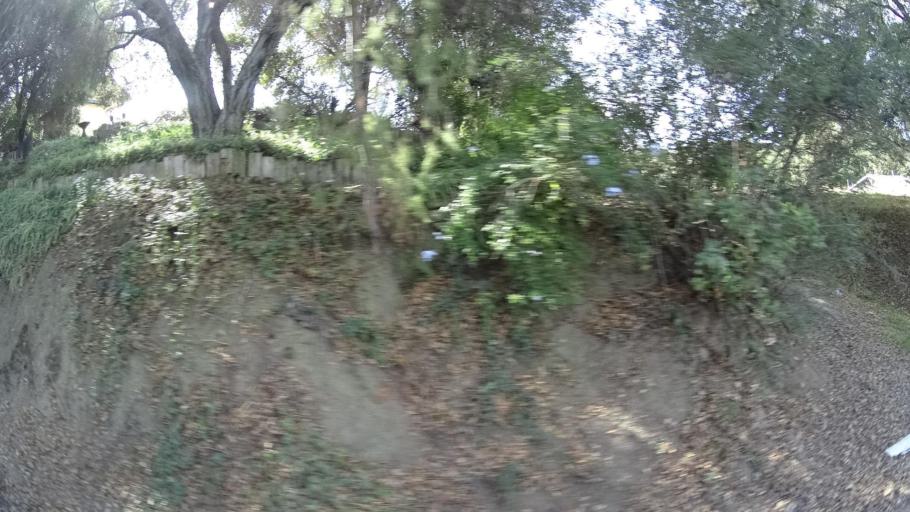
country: US
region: California
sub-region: San Diego County
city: Harbison Canyon
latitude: 32.8382
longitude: -116.8024
